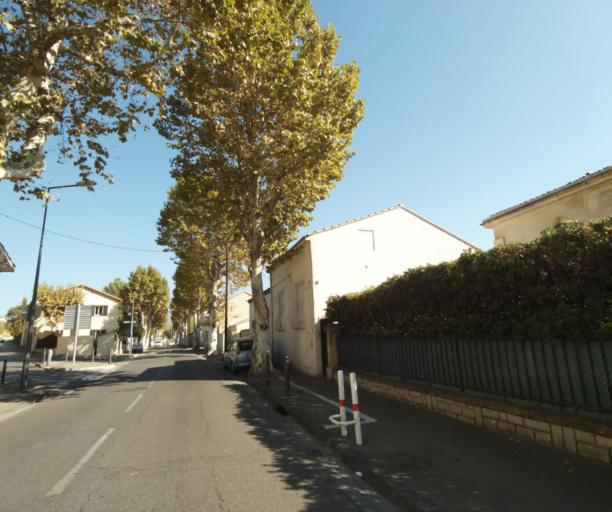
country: FR
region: Provence-Alpes-Cote d'Azur
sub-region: Departement des Bouches-du-Rhone
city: Plan-de-Cuques
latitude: 43.3366
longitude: 5.4521
